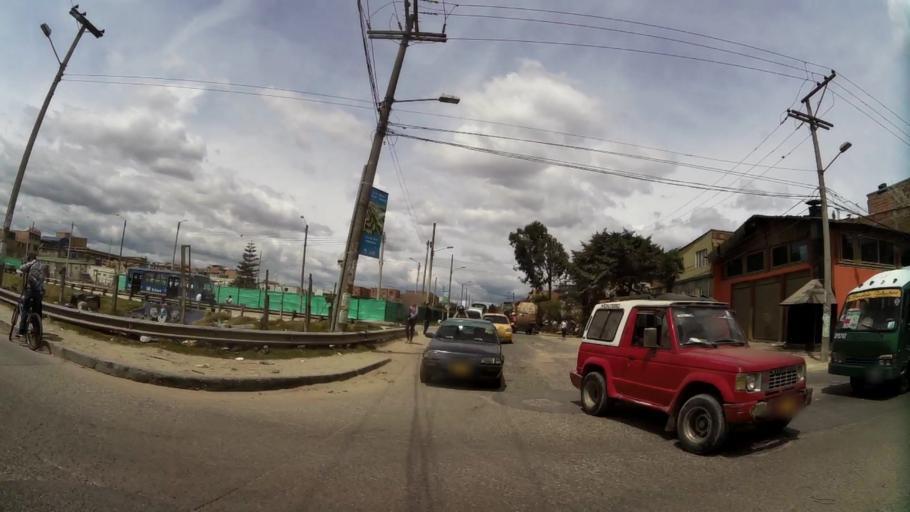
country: CO
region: Cundinamarca
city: Soacha
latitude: 4.6398
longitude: -74.1669
